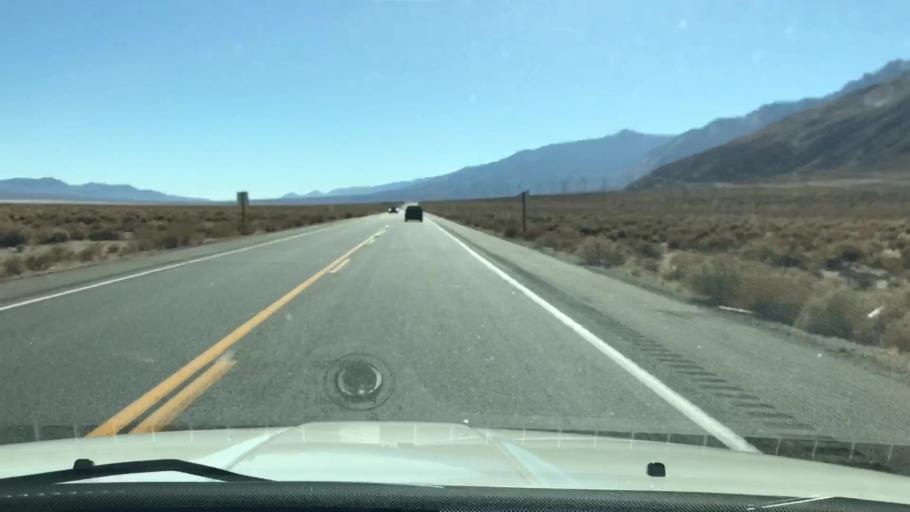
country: US
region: California
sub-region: Inyo County
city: Lone Pine
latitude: 36.3718
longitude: -118.0239
